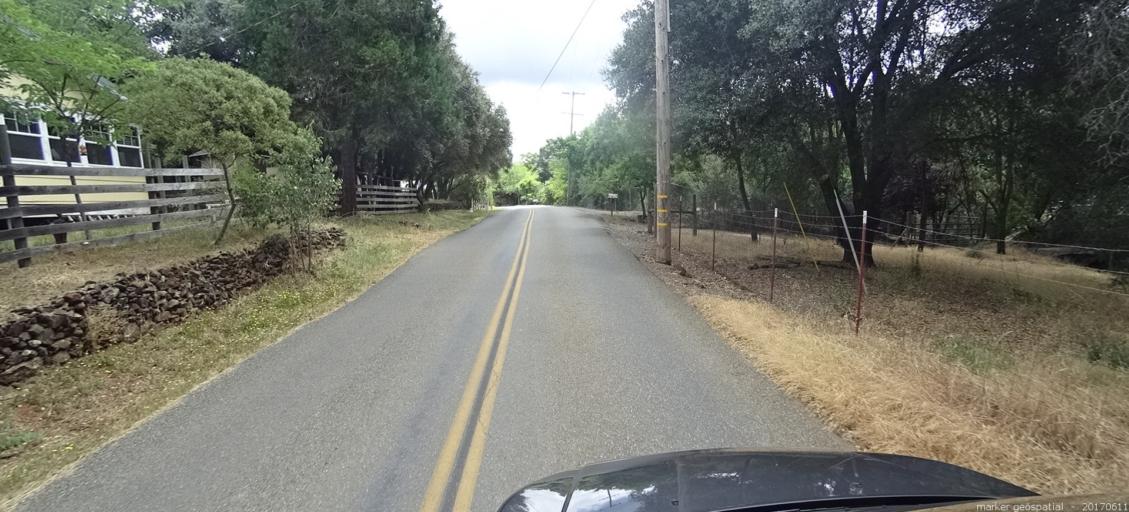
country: US
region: California
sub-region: Butte County
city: Oroville
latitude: 39.6426
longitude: -121.5431
